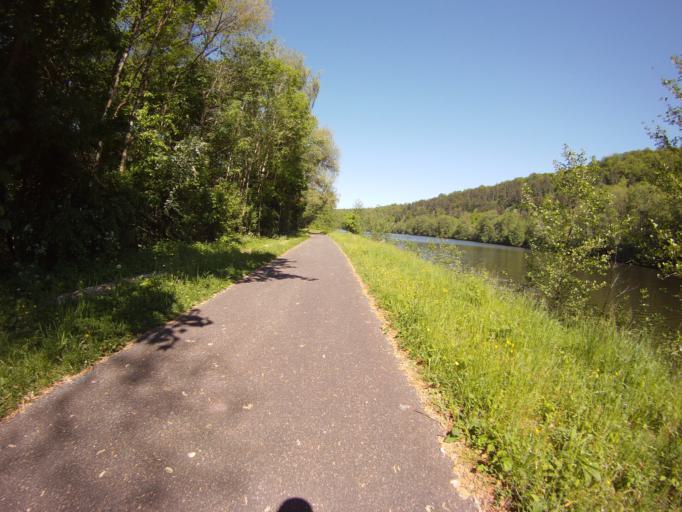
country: FR
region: Lorraine
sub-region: Departement de Meurthe-et-Moselle
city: Chaligny
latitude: 48.6509
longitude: 6.0373
